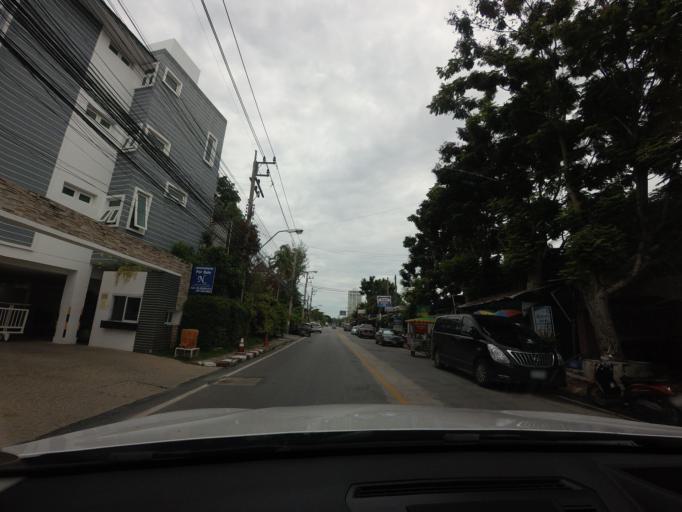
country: TH
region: Prachuap Khiri Khan
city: Hua Hin
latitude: 12.5245
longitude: 99.9743
